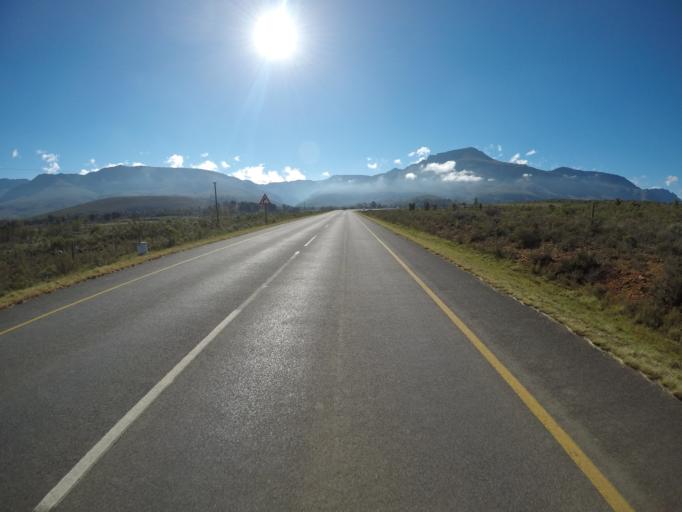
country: ZA
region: Western Cape
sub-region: Overberg District Municipality
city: Caledon
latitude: -34.0562
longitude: 19.5588
